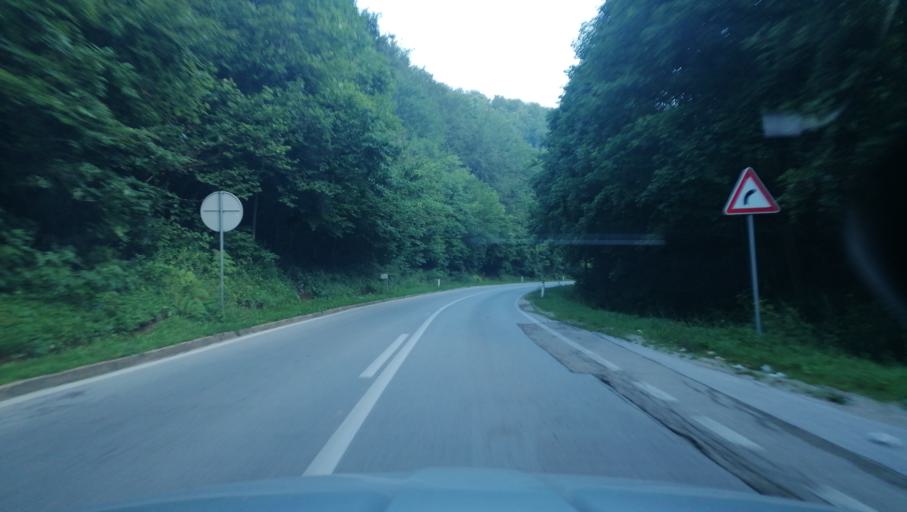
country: BA
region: Federation of Bosnia and Herzegovina
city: Prozor
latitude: 43.8707
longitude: 17.5944
